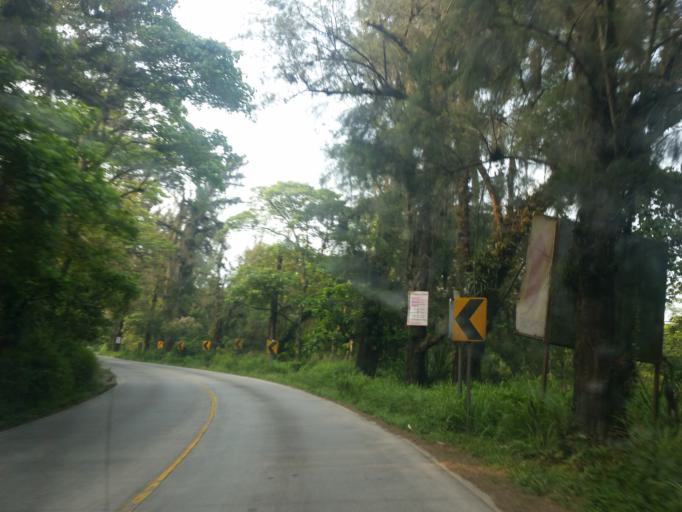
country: MX
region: Veracruz
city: Coatepec
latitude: 19.4319
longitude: -96.9561
